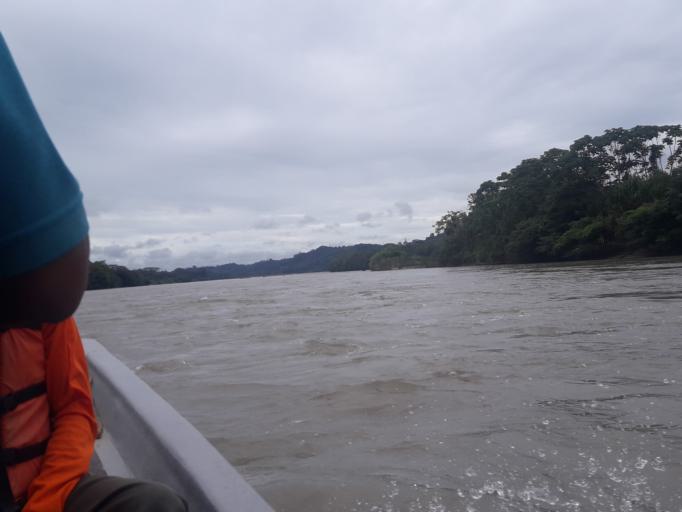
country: EC
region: Orellana
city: Boca Suno
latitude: -0.8818
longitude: -77.2988
